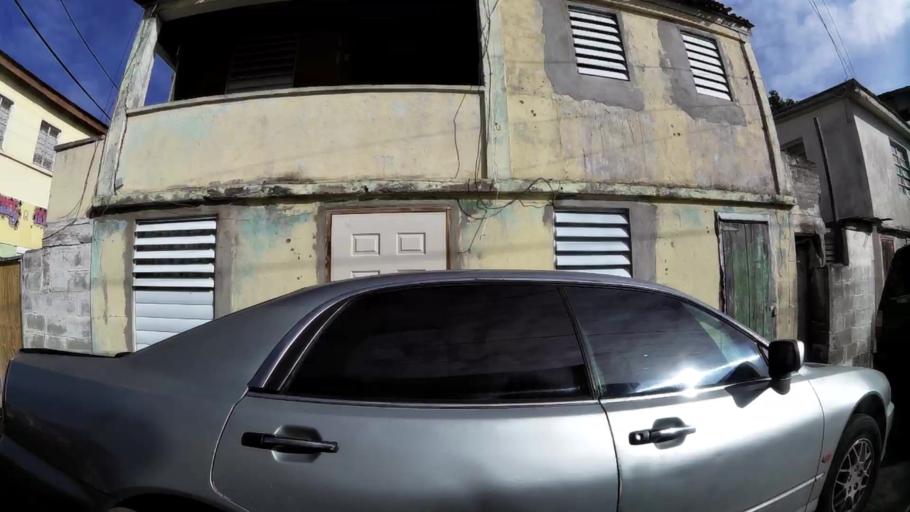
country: KN
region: Saint George Basseterre
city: Basseterre
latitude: 17.2944
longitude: -62.7277
